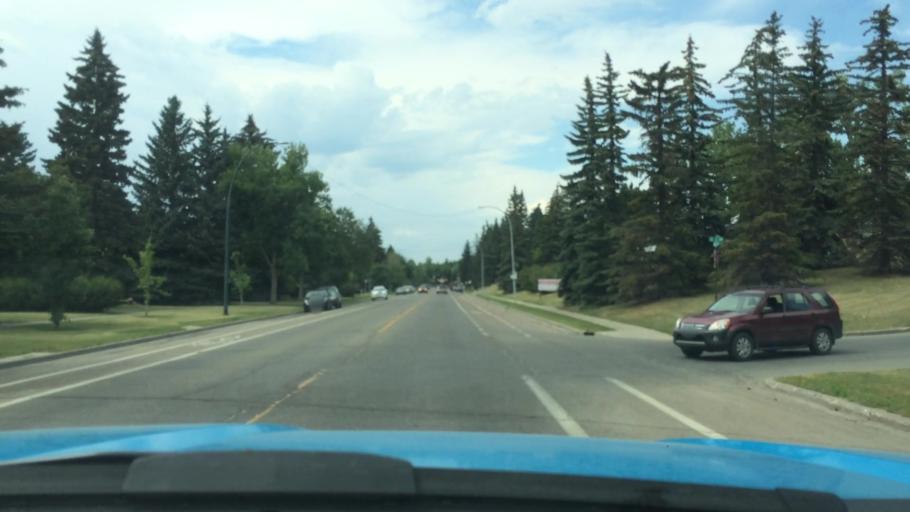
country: CA
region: Alberta
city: Calgary
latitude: 51.0795
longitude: -114.0870
